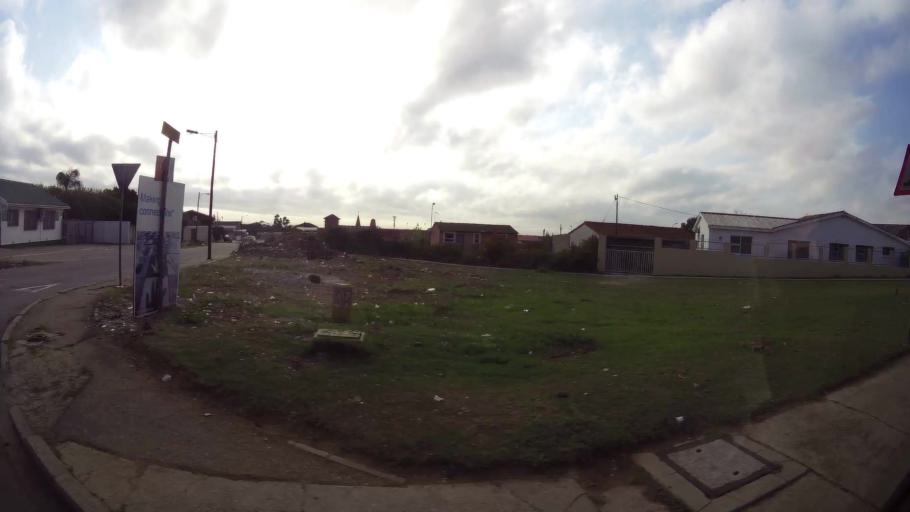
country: ZA
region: Eastern Cape
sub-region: Nelson Mandela Bay Metropolitan Municipality
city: Port Elizabeth
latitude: -33.9219
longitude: 25.5546
